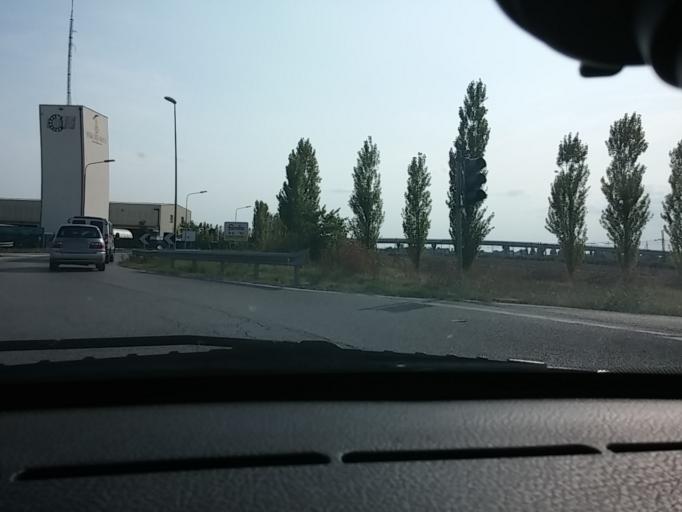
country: IT
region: Emilia-Romagna
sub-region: Provincia di Ferrara
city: Ferrara
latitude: 44.8277
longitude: 11.5924
